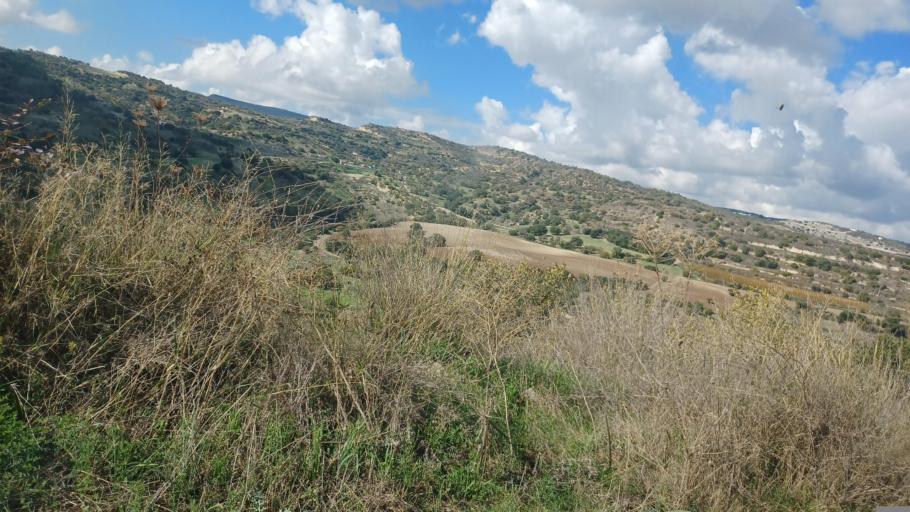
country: CY
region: Pafos
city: Mesogi
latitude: 34.8381
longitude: 32.5464
